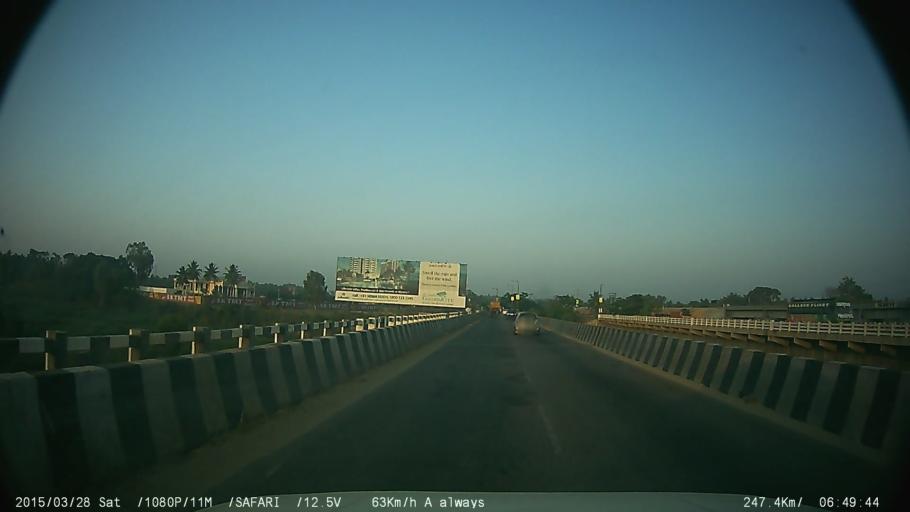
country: IN
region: Karnataka
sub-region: Mandya
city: Maddur
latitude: 12.6126
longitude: 77.0563
